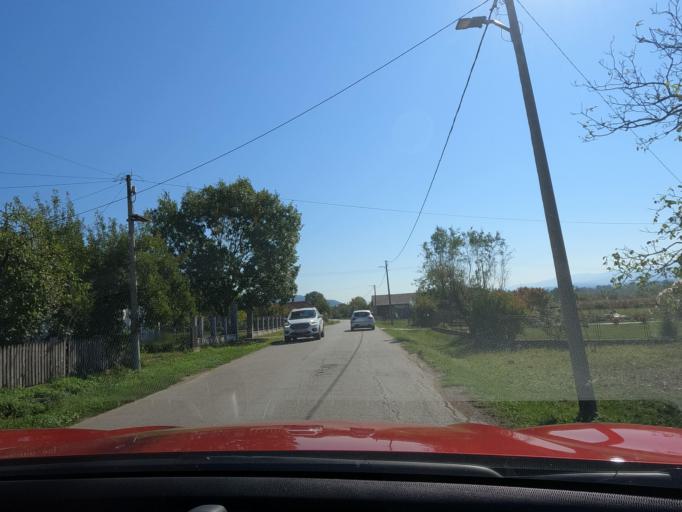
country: RS
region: Central Serbia
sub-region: Raski Okrug
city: Kraljevo
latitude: 43.7575
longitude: 20.6857
